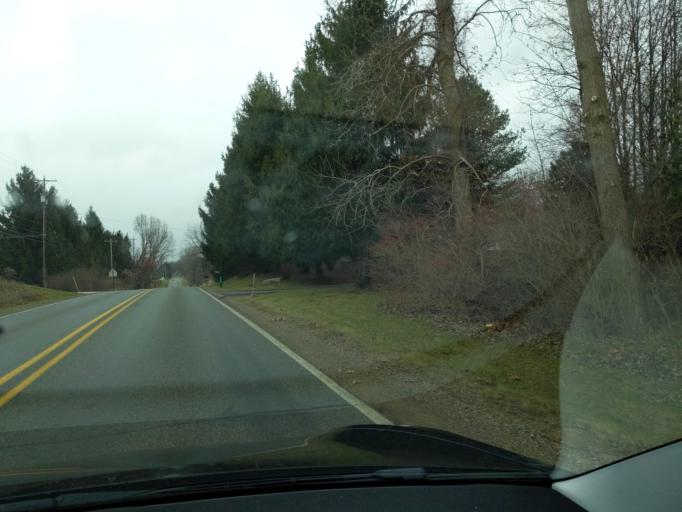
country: US
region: Michigan
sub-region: Jackson County
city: Spring Arbor
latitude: 42.2473
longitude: -84.5373
